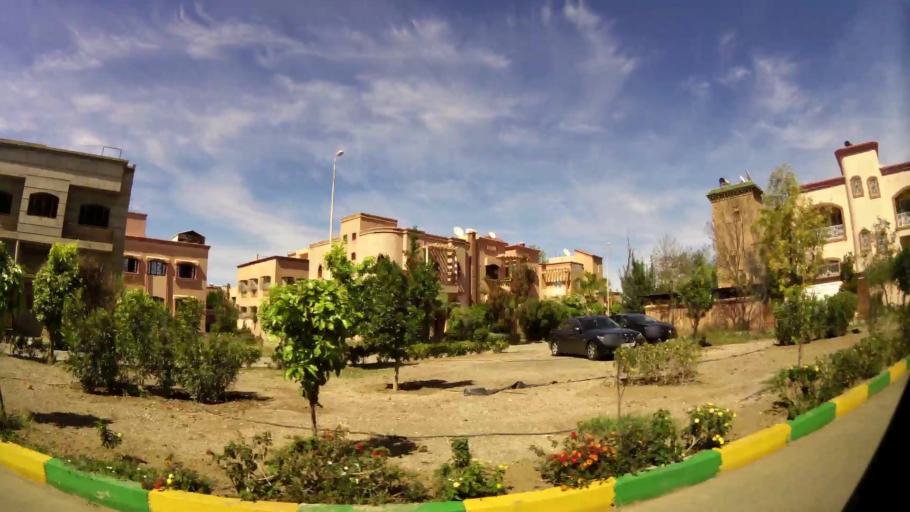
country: MA
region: Marrakech-Tensift-Al Haouz
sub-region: Marrakech
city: Marrakesh
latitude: 31.6786
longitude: -8.0047
